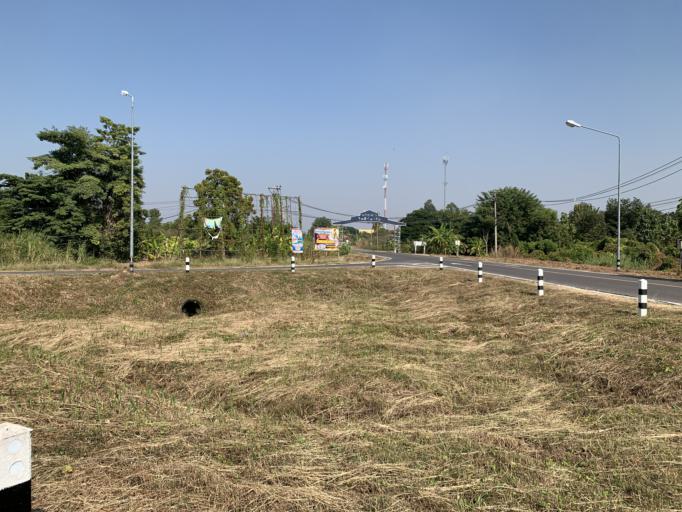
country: TH
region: Phichit
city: Phichit
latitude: 16.3440
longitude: 100.3926
